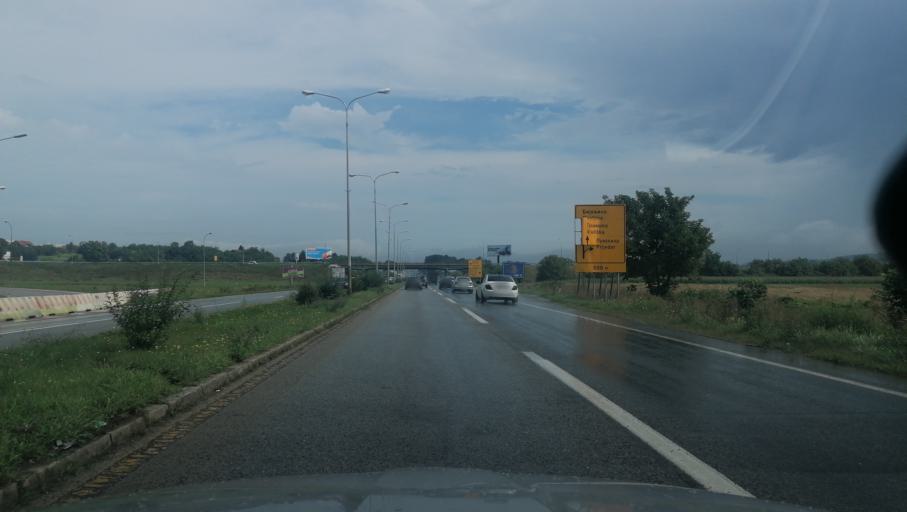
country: BA
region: Republika Srpska
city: Banja Luka
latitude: 44.8169
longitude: 17.2018
